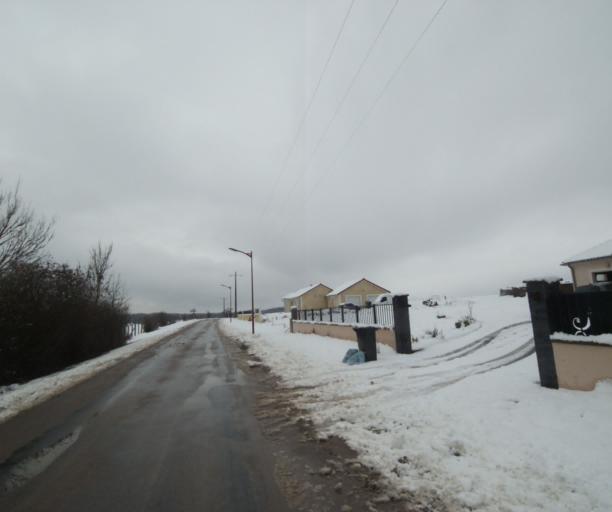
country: FR
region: Champagne-Ardenne
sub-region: Departement de la Haute-Marne
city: Laneuville-a-Remy
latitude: 48.4765
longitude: 4.8836
